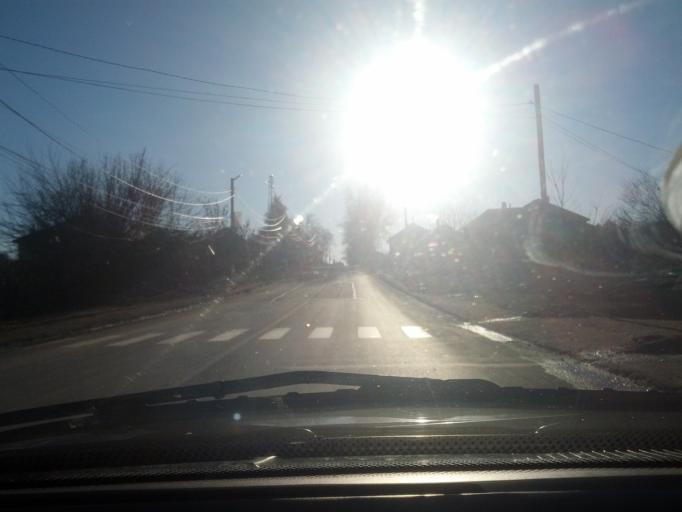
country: BG
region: Vratsa
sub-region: Obshtina Miziya
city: Miziya
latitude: 43.6981
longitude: 23.8174
